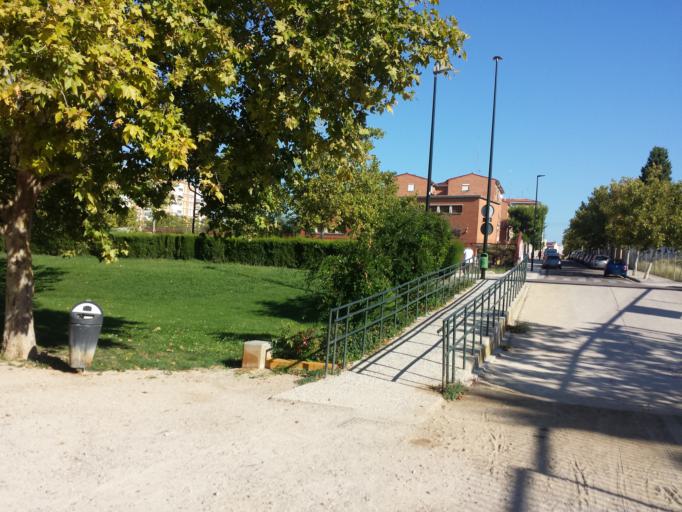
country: ES
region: Aragon
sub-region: Provincia de Zaragoza
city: Oliver-Valdefierro, Oliver, Valdefierro
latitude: 41.6494
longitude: -0.9284
